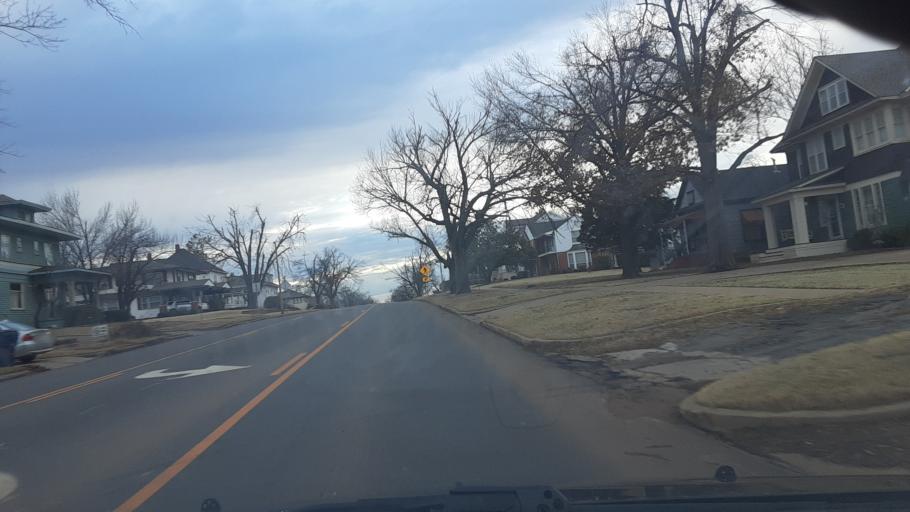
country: US
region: Oklahoma
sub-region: Logan County
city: Guthrie
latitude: 35.8802
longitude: -97.4156
